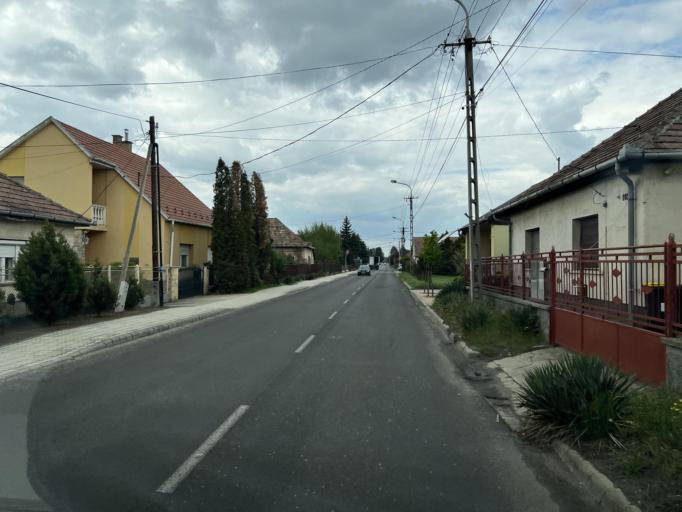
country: HU
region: Pest
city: Hernad
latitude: 47.1684
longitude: 19.4206
